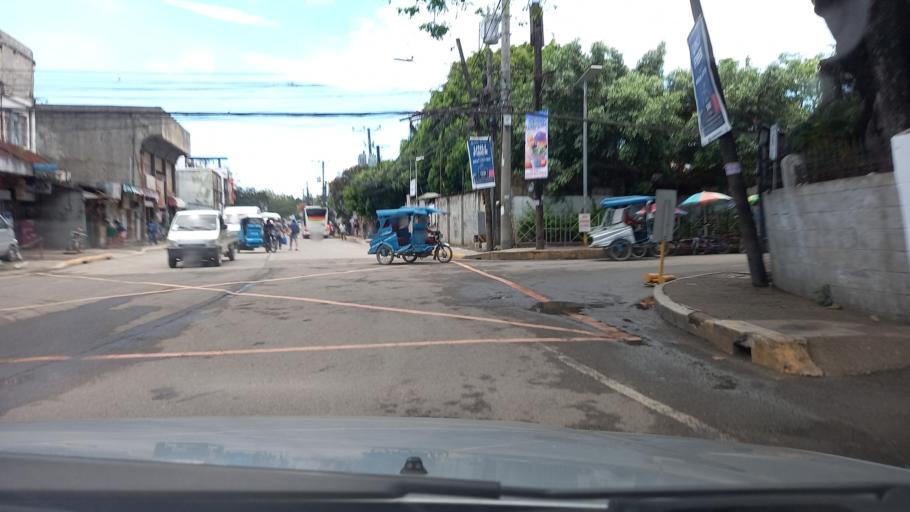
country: PH
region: Central Visayas
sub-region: Lapu-Lapu City
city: Buagsong
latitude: 10.3270
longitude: 123.9424
